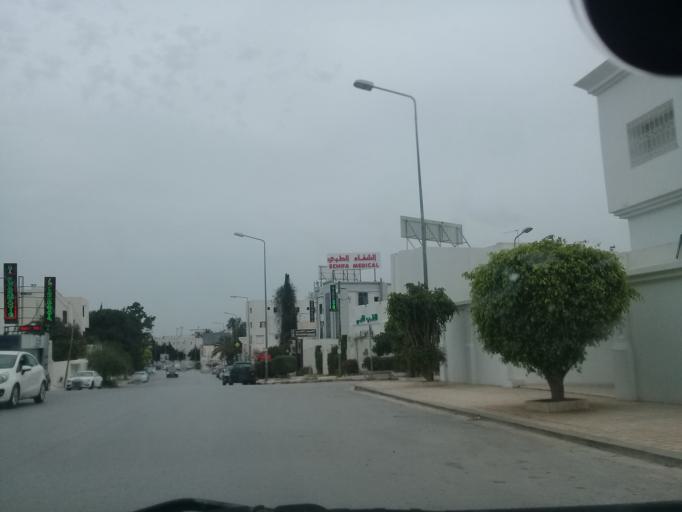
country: TN
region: Tunis
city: Tunis
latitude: 36.8420
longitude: 10.1596
